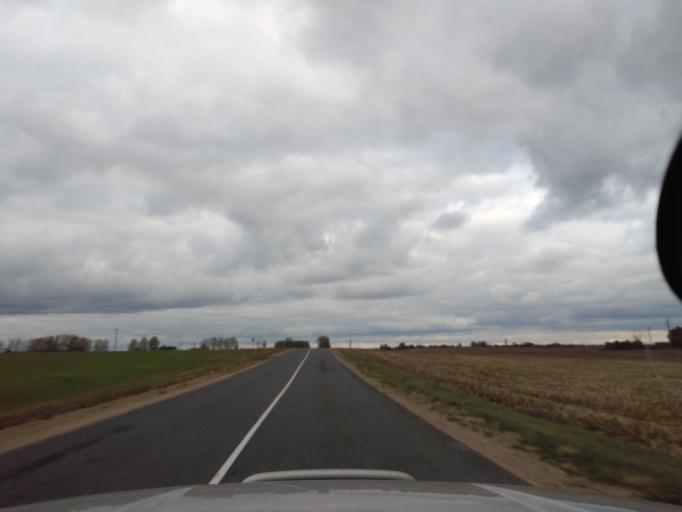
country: BY
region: Minsk
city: Kapyl'
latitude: 53.1653
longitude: 27.3100
